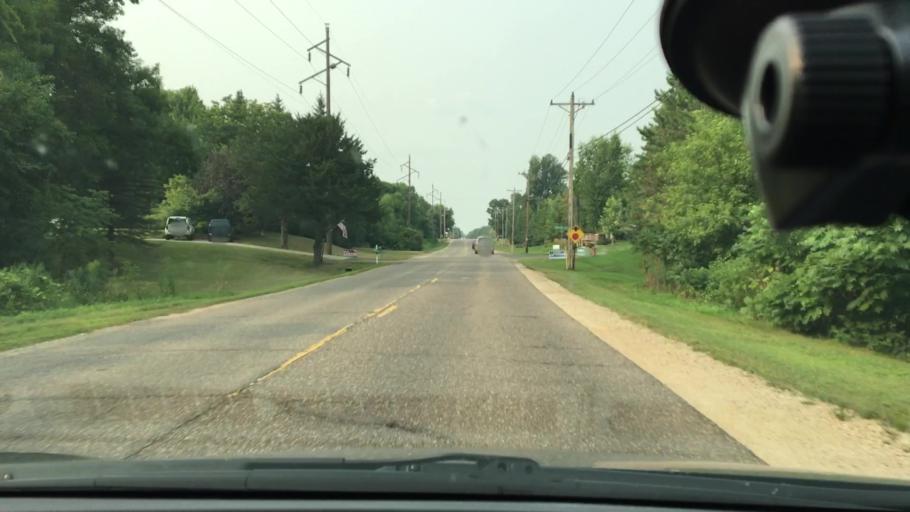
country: US
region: Minnesota
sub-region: Hennepin County
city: Champlin
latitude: 45.1964
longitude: -93.4424
